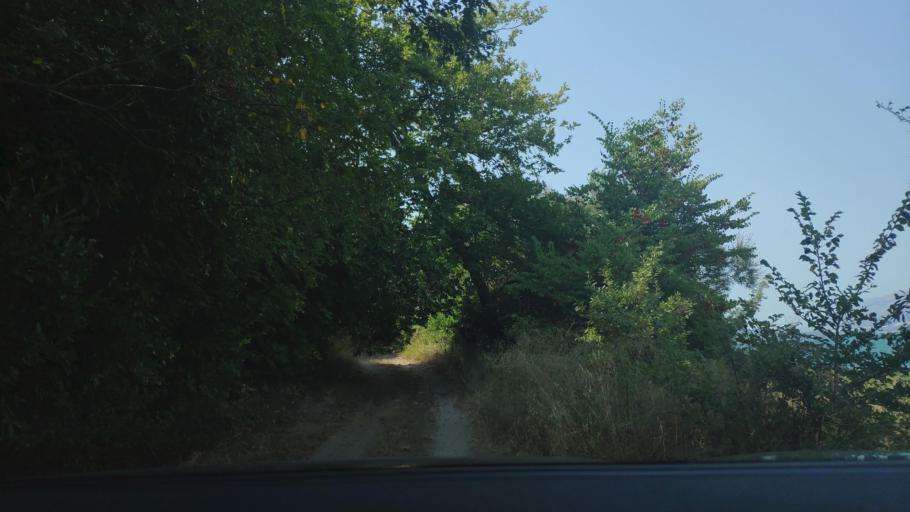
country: GR
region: West Greece
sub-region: Nomos Aitolias kai Akarnanias
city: Fitiai
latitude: 38.7290
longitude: 21.1854
